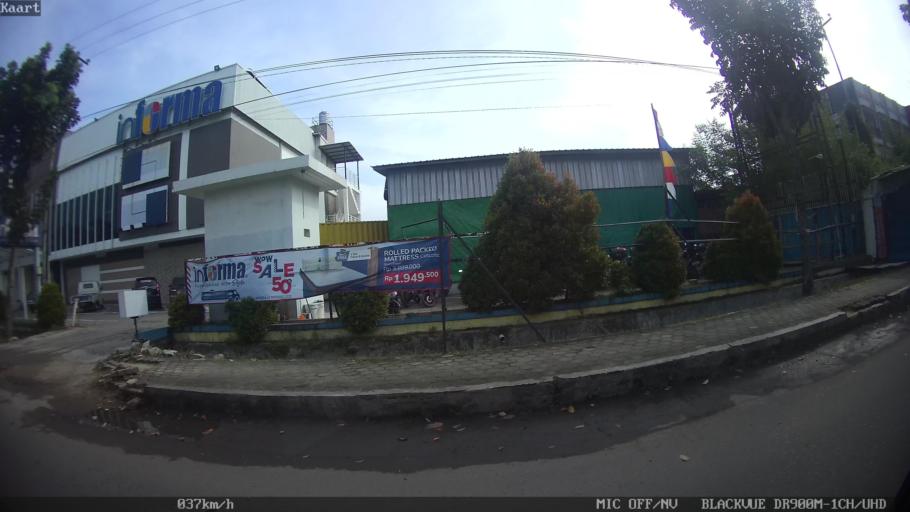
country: ID
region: Lampung
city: Kedaton
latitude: -5.3822
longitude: 105.2764
